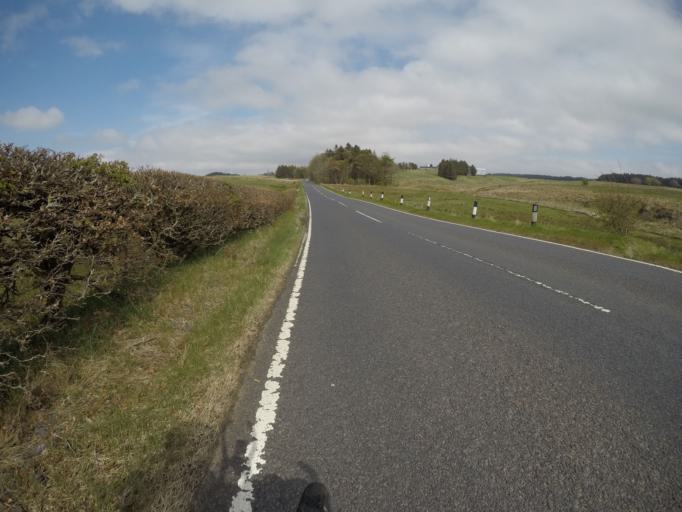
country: GB
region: Scotland
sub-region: East Renfrewshire
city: Neilston
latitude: 55.7178
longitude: -4.4357
